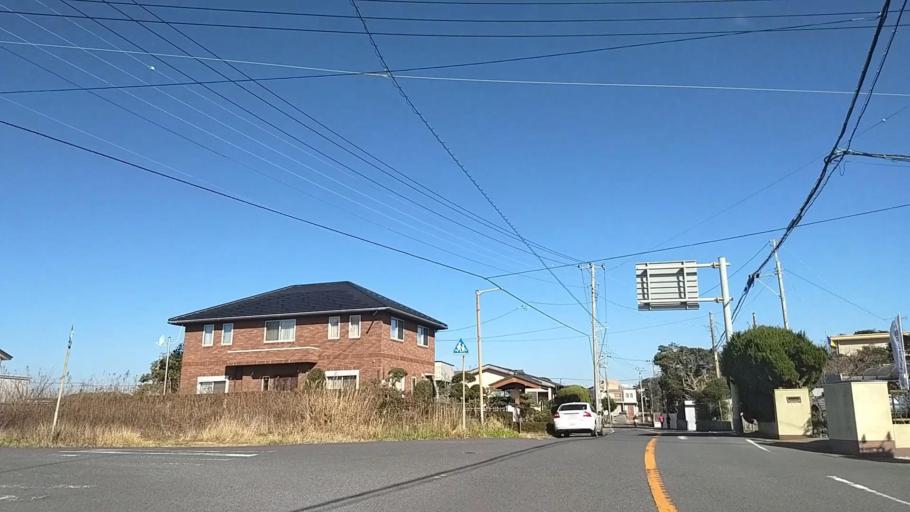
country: JP
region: Chiba
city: Hasaki
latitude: 35.7037
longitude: 140.8612
